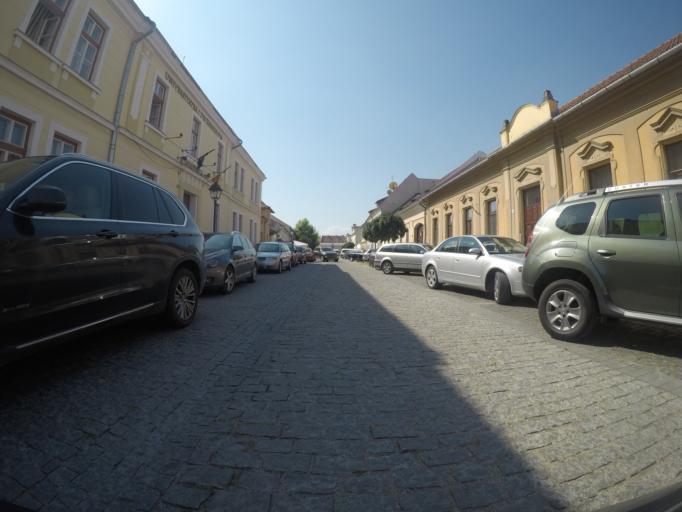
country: RO
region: Alba
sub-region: Municipiul Alba Iulia
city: Alba Iulia
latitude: 46.0699
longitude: 23.5718
